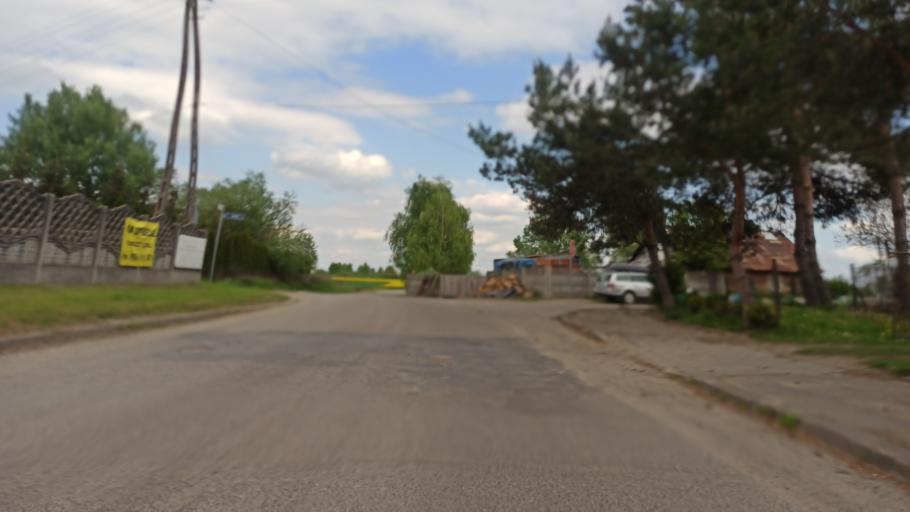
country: PL
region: Subcarpathian Voivodeship
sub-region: Powiat jaroslawski
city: Radymno
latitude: 49.9564
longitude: 22.8196
